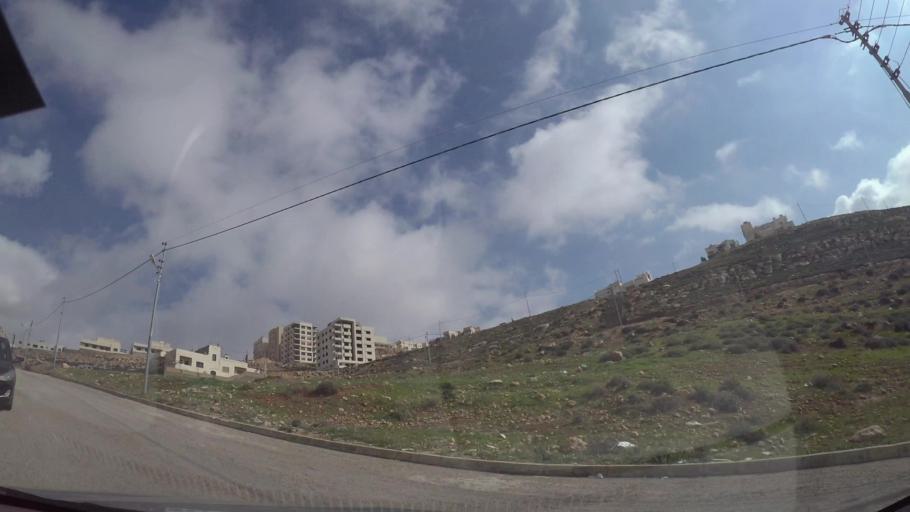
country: JO
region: Amman
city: Al Jubayhah
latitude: 32.0586
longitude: 35.8656
